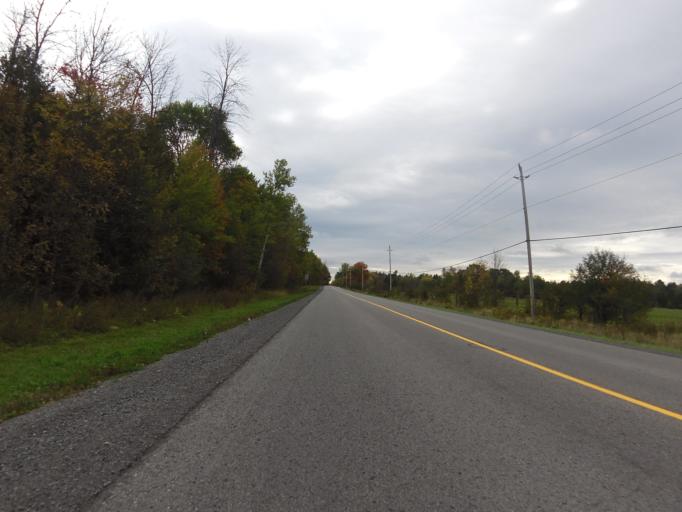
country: CA
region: Ontario
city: Arnprior
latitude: 45.4346
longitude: -76.1121
